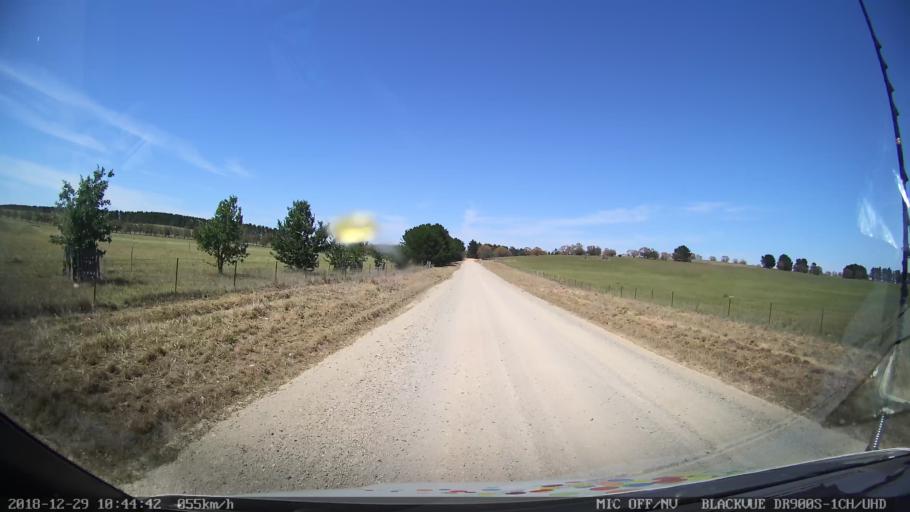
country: AU
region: New South Wales
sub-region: Palerang
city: Bungendore
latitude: -35.0433
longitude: 149.5267
